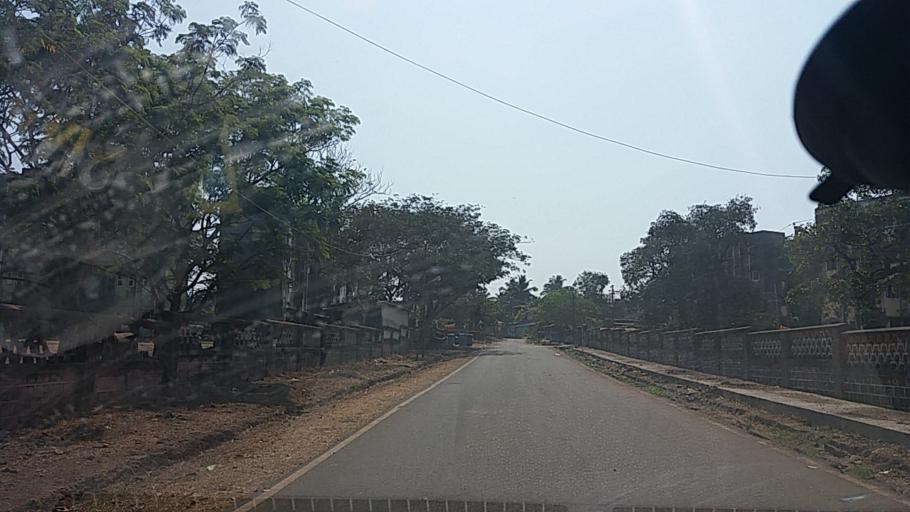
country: IN
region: Goa
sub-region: South Goa
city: Marmagao
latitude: 15.4080
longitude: 73.7903
